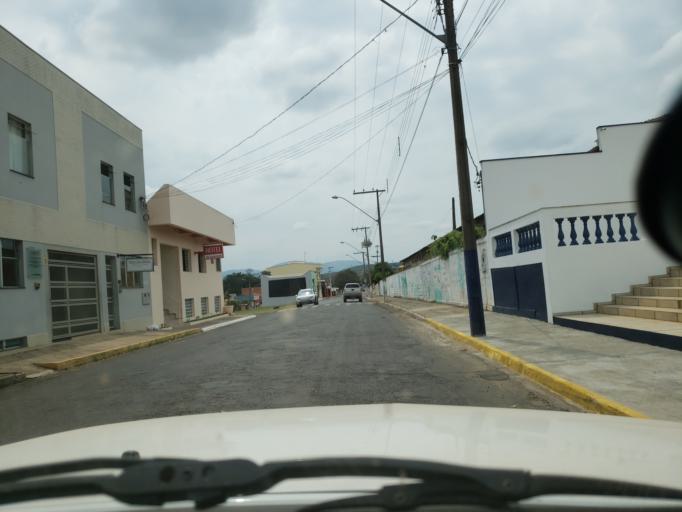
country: BR
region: Minas Gerais
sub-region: Jacutinga
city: Jacutinga
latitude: -22.2802
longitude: -46.6076
